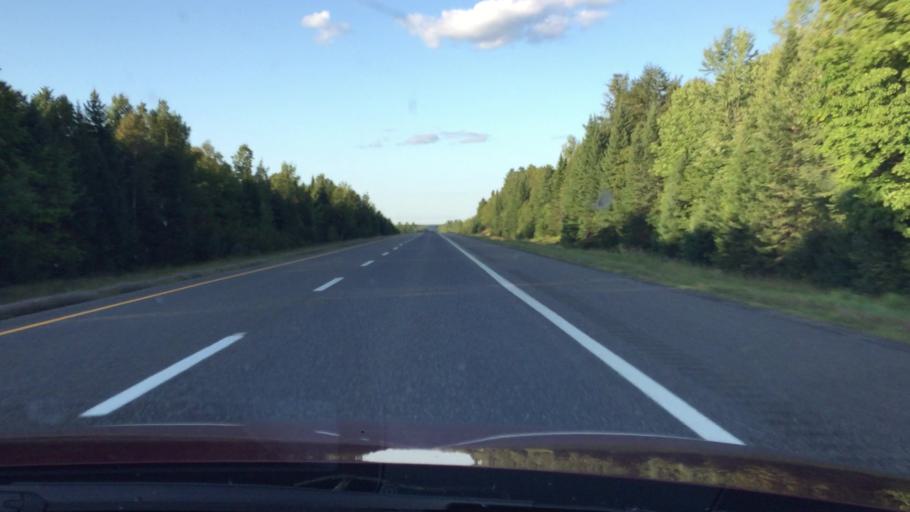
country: US
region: Maine
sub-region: Penobscot County
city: Patten
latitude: 46.0577
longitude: -68.2357
